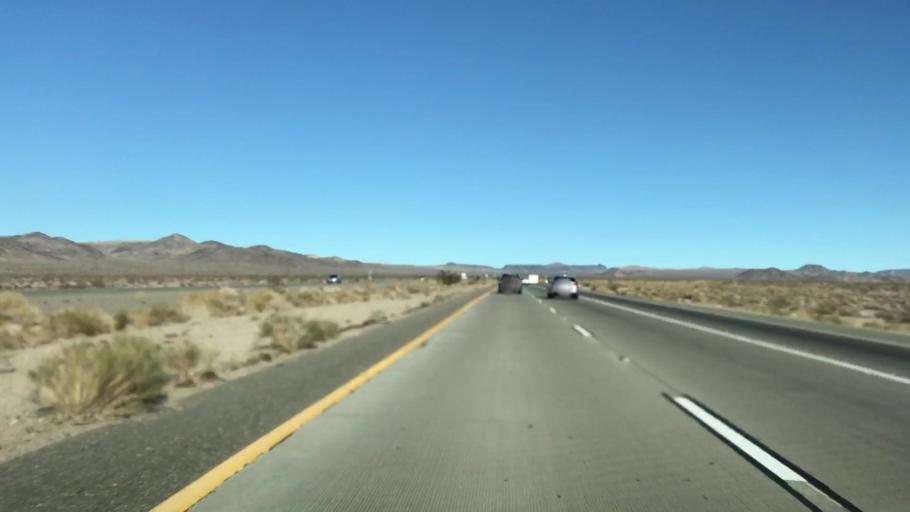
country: US
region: Nevada
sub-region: Clark County
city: Sandy Valley
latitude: 35.3151
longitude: -115.9962
